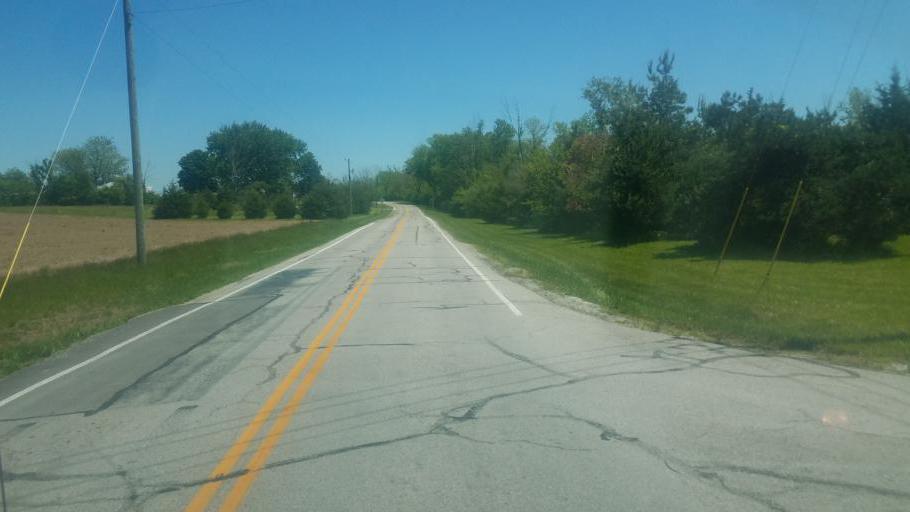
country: US
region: Ohio
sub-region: Miami County
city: Piqua
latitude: 40.2118
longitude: -84.2898
